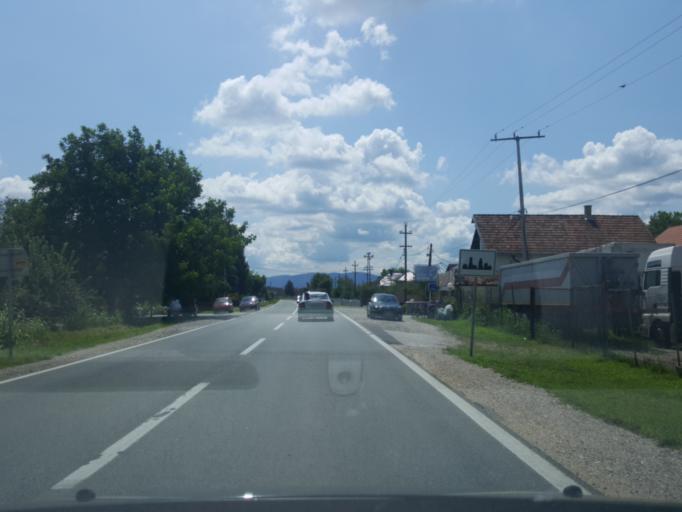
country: RS
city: Kozjak
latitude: 44.6208
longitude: 19.2673
